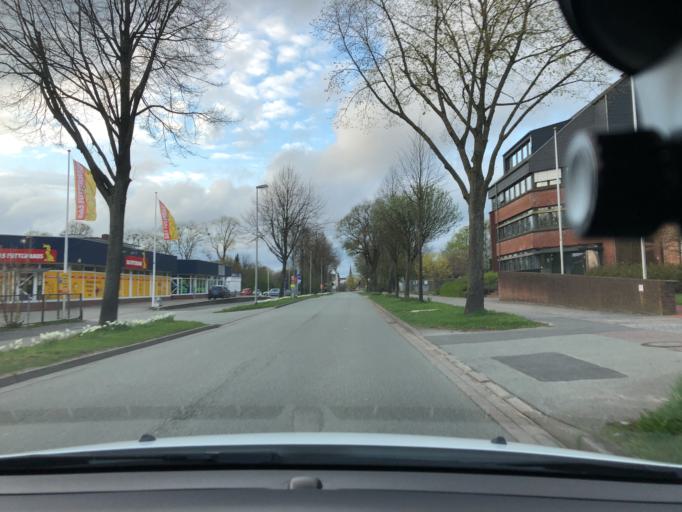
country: DE
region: Schleswig-Holstein
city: Flensburg
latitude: 54.7721
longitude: 9.4352
